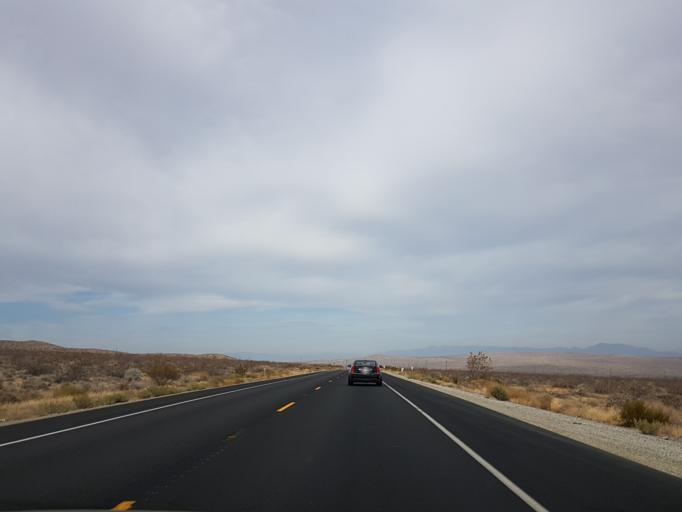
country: US
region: California
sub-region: Kern County
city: Ridgecrest
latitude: 35.4681
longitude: -117.6546
